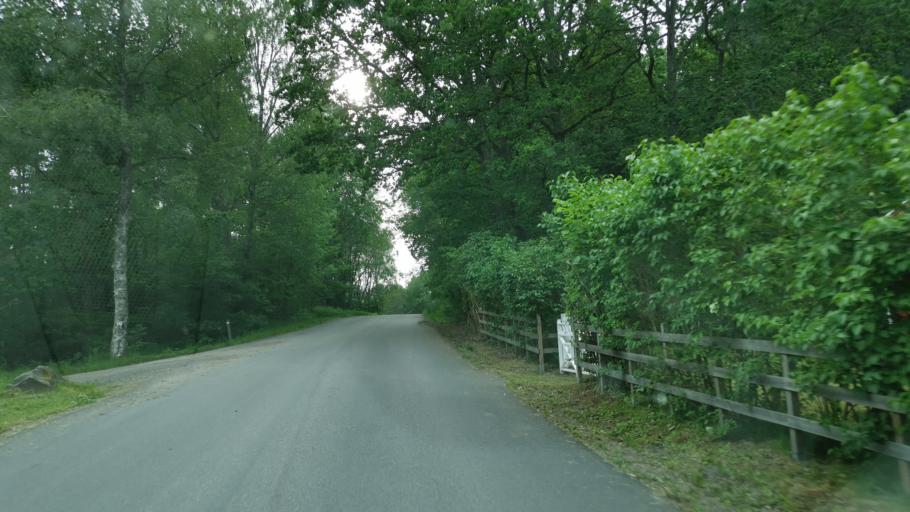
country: SE
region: Vaestra Goetaland
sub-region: Vanersborgs Kommun
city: Vargon
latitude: 58.3591
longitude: 12.3638
